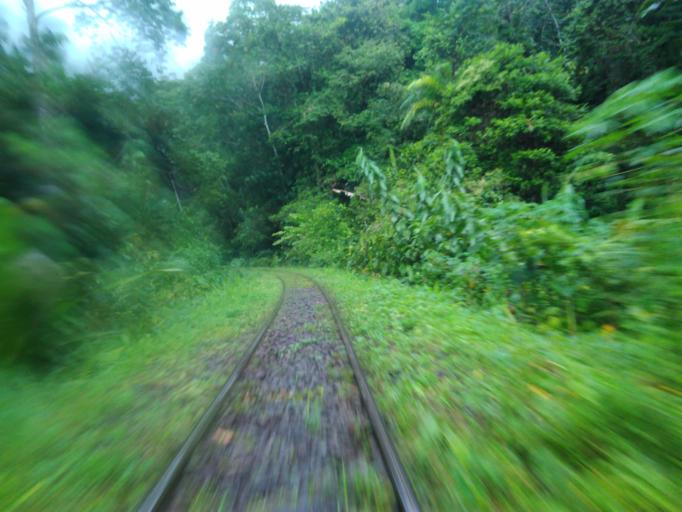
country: CO
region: Valle del Cauca
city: Buenaventura
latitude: 3.8448
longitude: -76.8819
